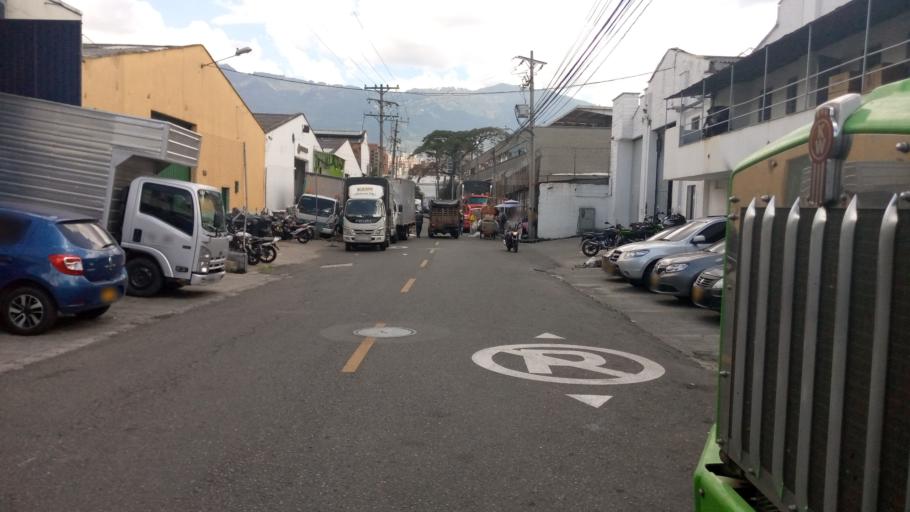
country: CO
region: Antioquia
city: Envigado
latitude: 6.1812
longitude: -75.5934
